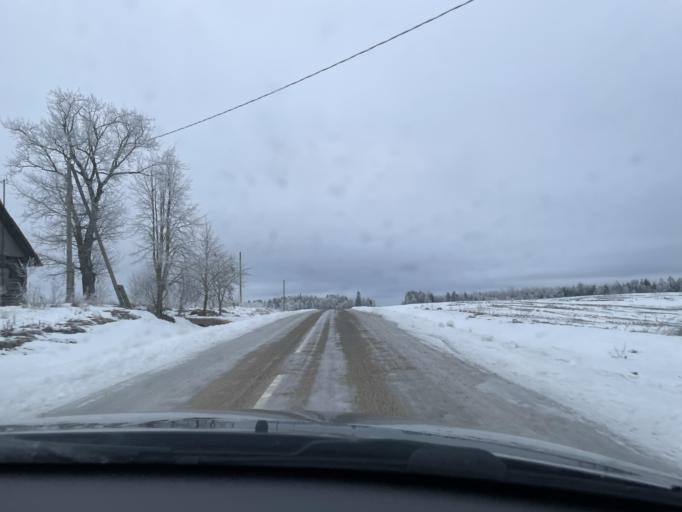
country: LV
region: Ludzas Rajons
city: Ludza
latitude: 56.4445
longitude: 27.5428
